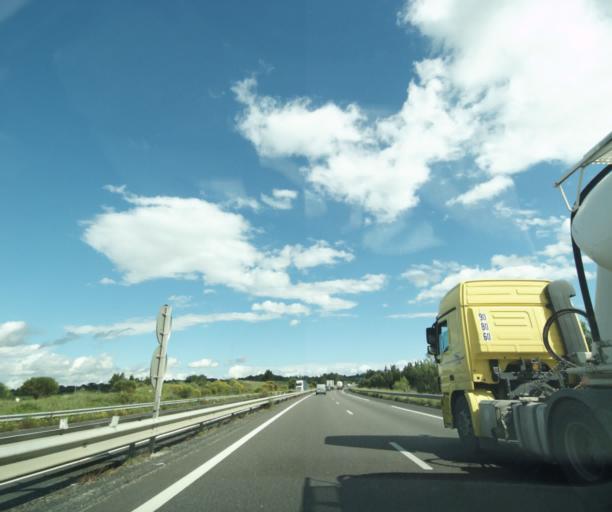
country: FR
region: Languedoc-Roussillon
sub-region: Departement du Gard
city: Caissargues
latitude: 43.7945
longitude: 4.3937
